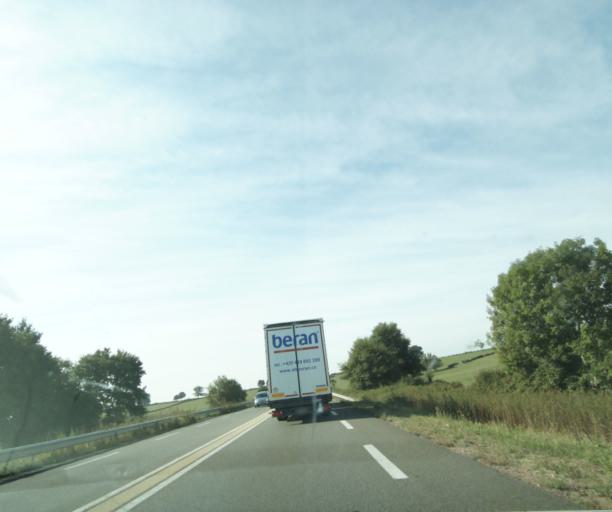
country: FR
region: Bourgogne
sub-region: Departement de Saone-et-Loire
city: Genelard
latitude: 46.5867
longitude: 4.2222
